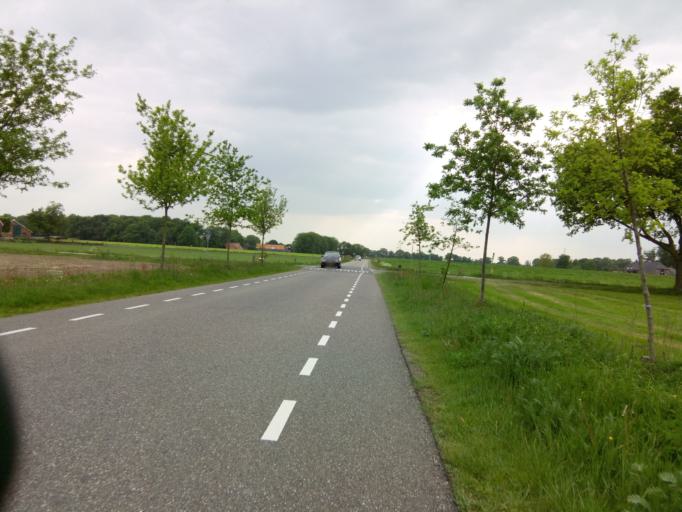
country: NL
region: Gelderland
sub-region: Berkelland
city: Eibergen
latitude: 52.0809
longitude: 6.6090
